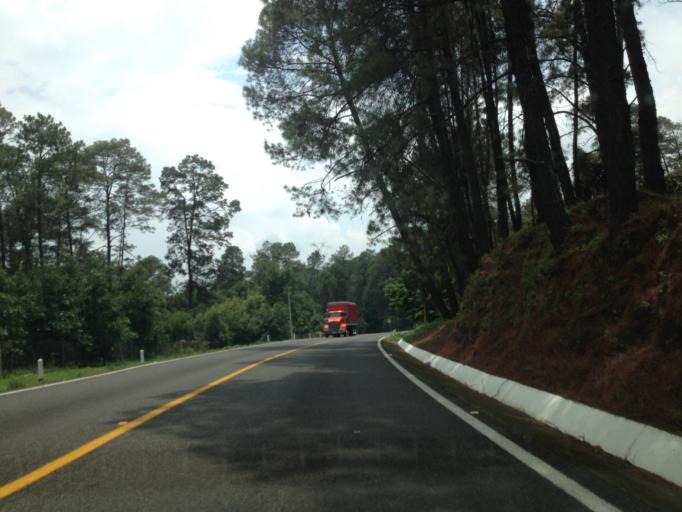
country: MX
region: Michoacan
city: Tingambato
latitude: 19.4759
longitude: -101.9239
